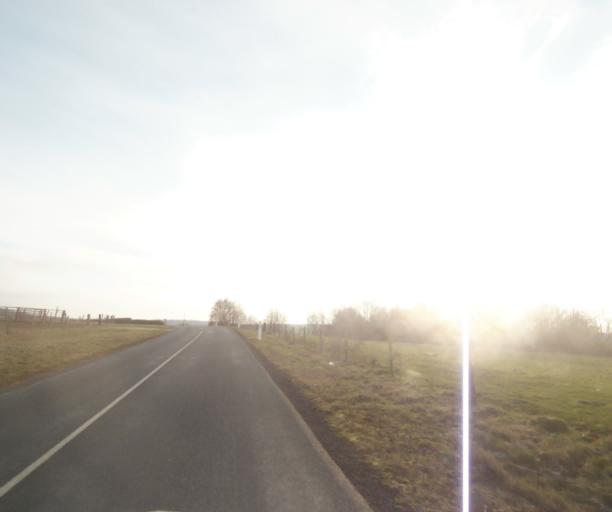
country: FR
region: Champagne-Ardenne
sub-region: Departement de la Marne
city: Sermaize-les-Bains
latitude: 48.7355
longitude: 4.9178
